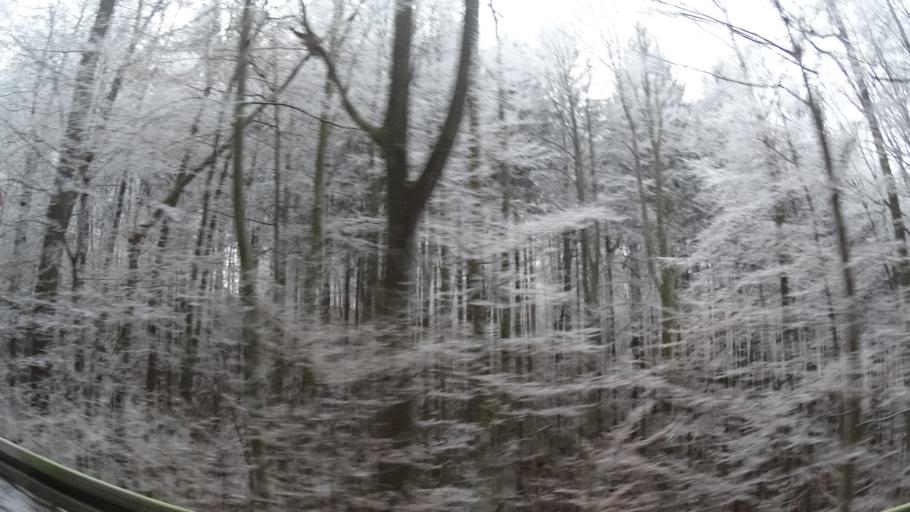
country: DE
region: Bavaria
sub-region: Regierungsbezirk Unterfranken
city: Johannesberg
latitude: 50.0479
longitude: 9.1099
